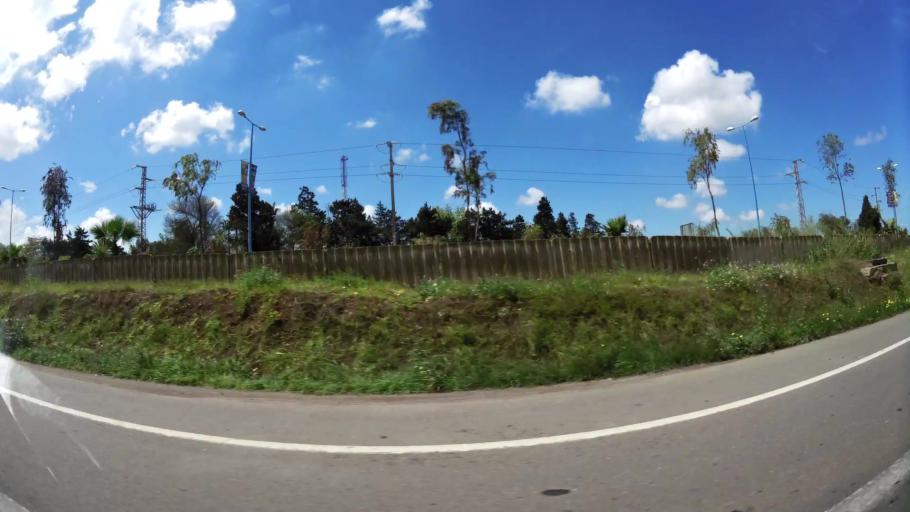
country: MA
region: Grand Casablanca
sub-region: Nouaceur
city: Bouskoura
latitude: 33.4954
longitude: -7.6291
